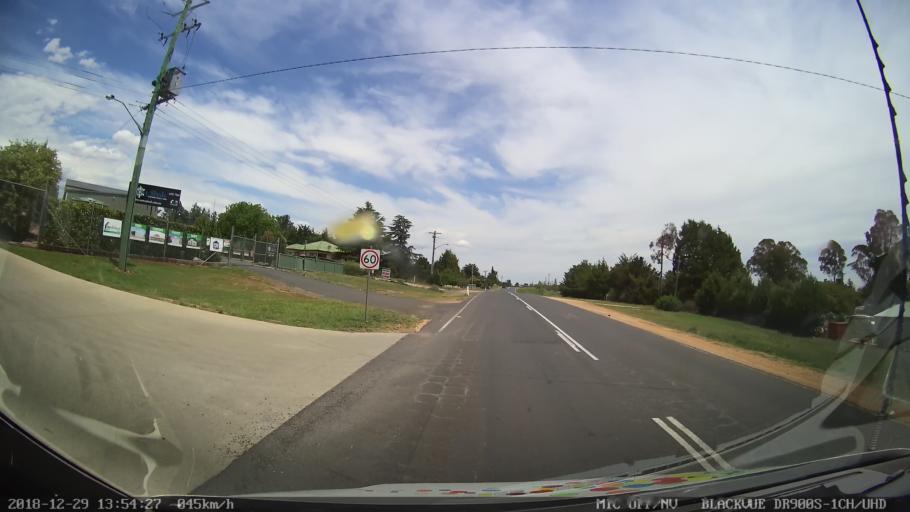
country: AU
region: New South Wales
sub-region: Cooma-Monaro
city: Cooma
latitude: -36.2143
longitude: 149.1519
